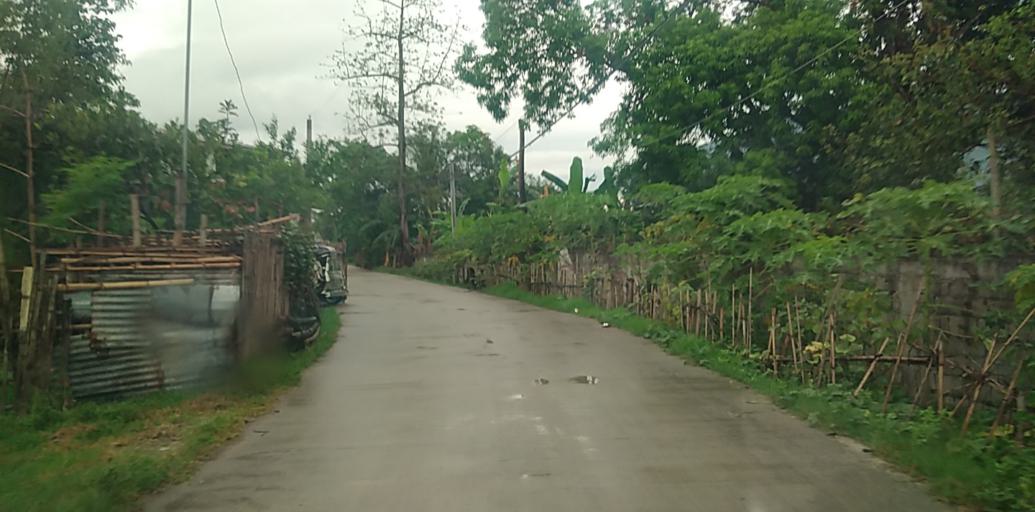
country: PH
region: Central Luzon
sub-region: Province of Pampanga
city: Anao
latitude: 15.1491
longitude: 120.7248
